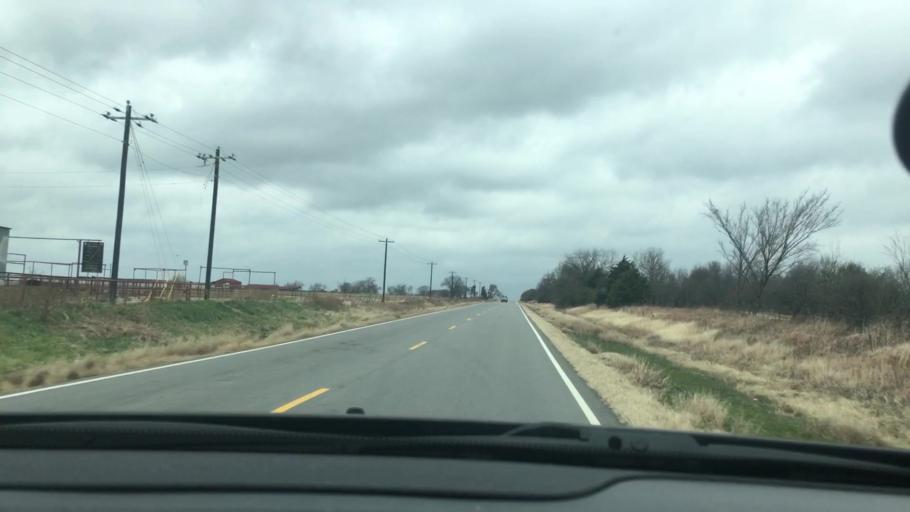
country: US
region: Oklahoma
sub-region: Atoka County
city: Atoka
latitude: 34.3749
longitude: -96.2415
